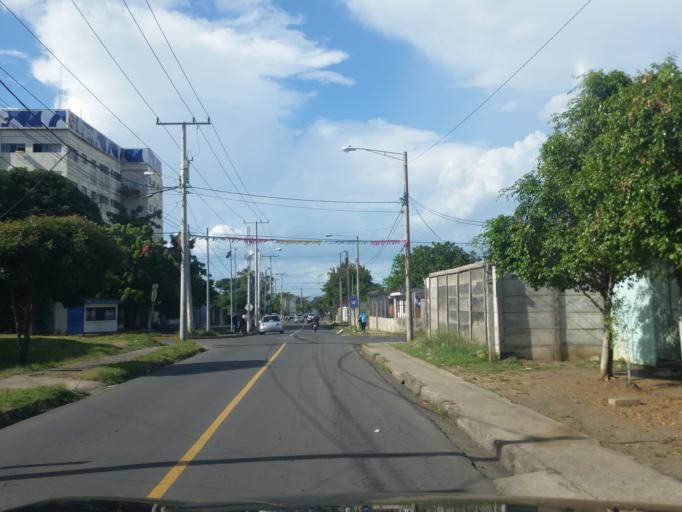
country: NI
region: Managua
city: Managua
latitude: 12.1519
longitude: -86.2680
